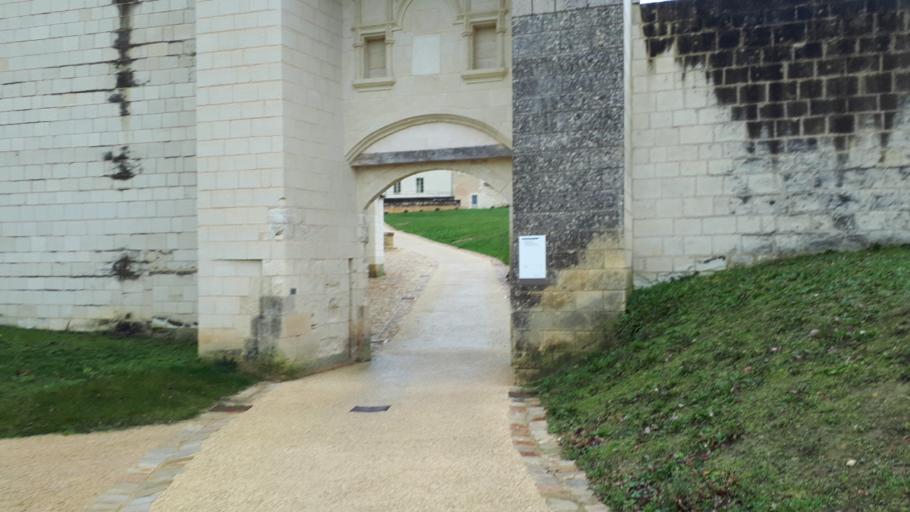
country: FR
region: Pays de la Loire
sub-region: Departement de Maine-et-Loire
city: Fontevraud-l'Abbaye
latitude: 47.1817
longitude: 0.0528
